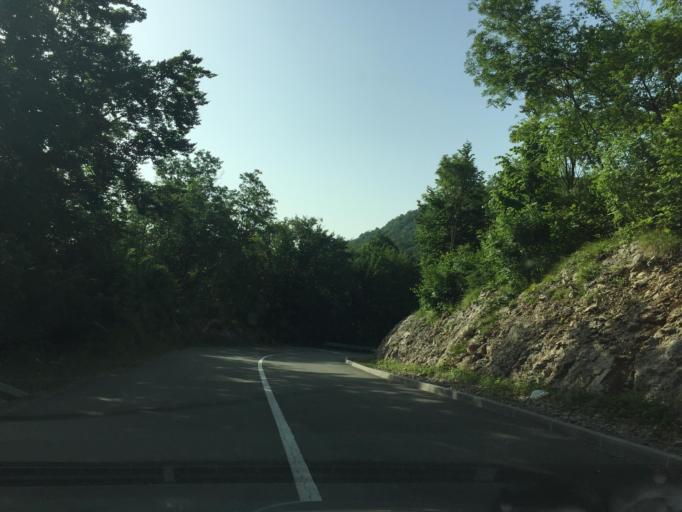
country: HR
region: Primorsko-Goranska
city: Matulji
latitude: 45.4083
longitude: 14.2536
